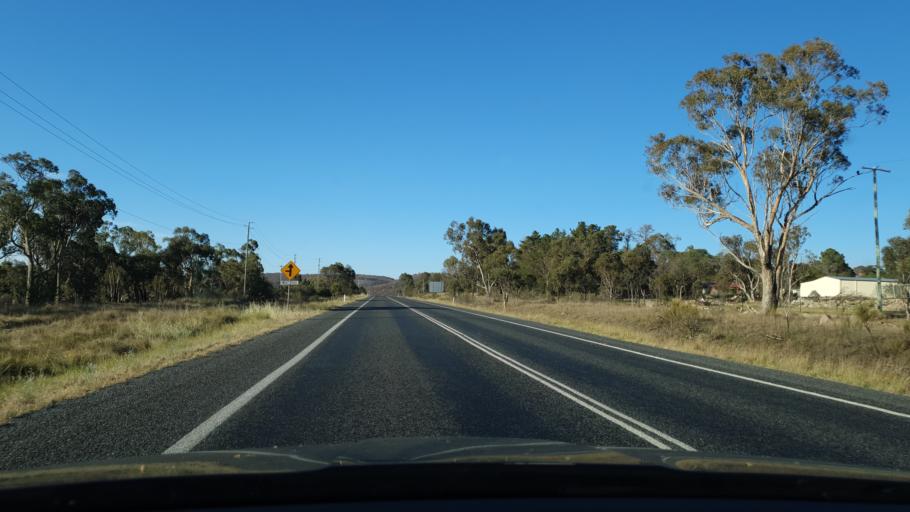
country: AU
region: Queensland
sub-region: Southern Downs
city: Stanthorpe
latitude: -28.6644
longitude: 151.9156
